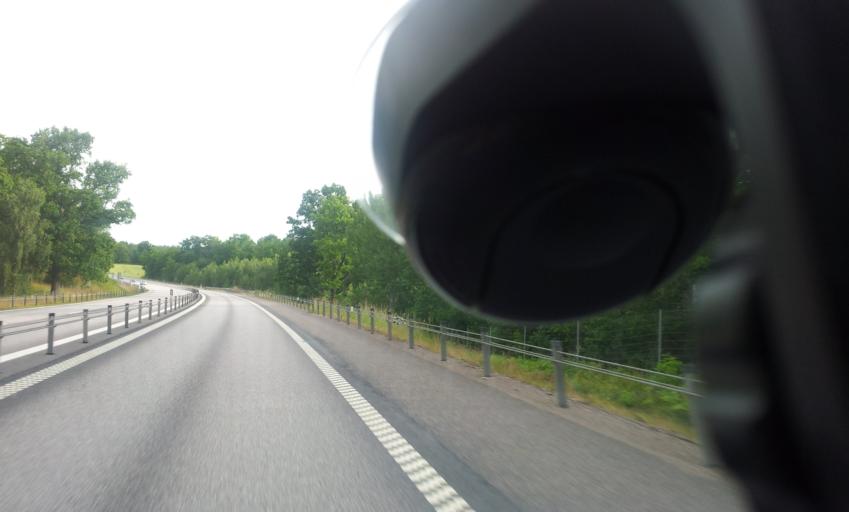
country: SE
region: OEstergoetland
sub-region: Valdemarsviks Kommun
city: Gusum
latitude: 58.3512
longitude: 16.4471
